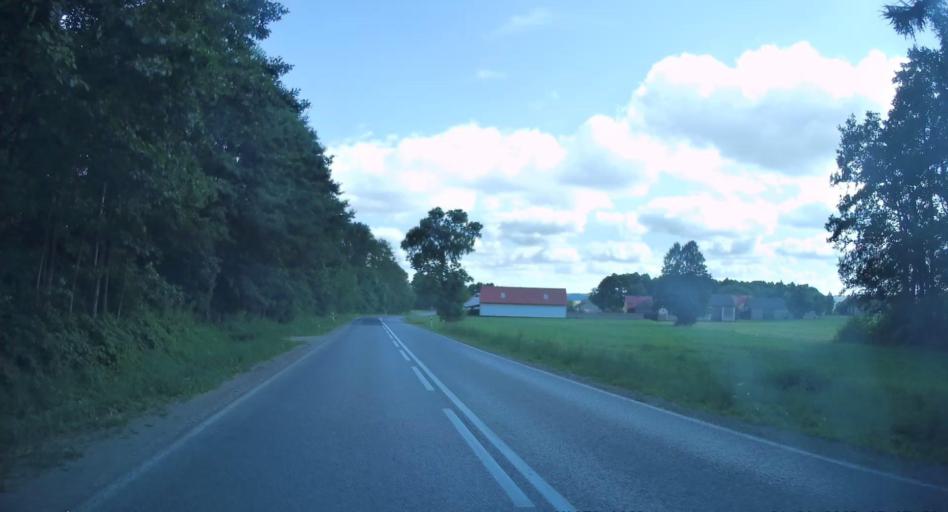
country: PL
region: Swietokrzyskie
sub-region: Powiat kielecki
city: Lagow
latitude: 50.8028
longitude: 21.0806
